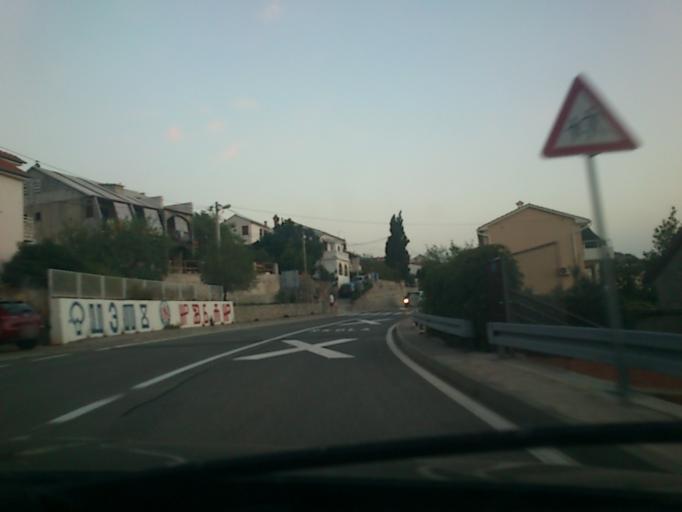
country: HR
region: Licko-Senjska
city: Senj
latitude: 44.9298
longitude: 14.9215
